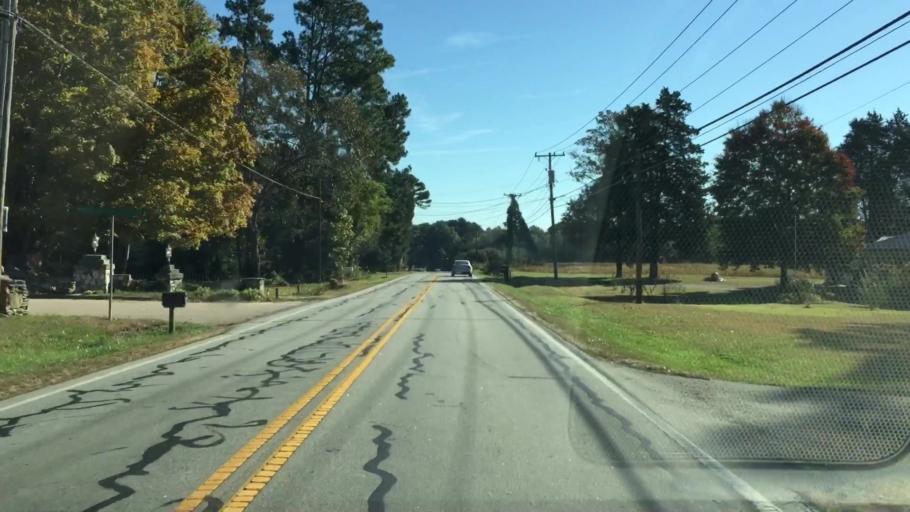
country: US
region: North Carolina
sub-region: Rowan County
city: Salisbury
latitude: 35.6613
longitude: -80.5407
